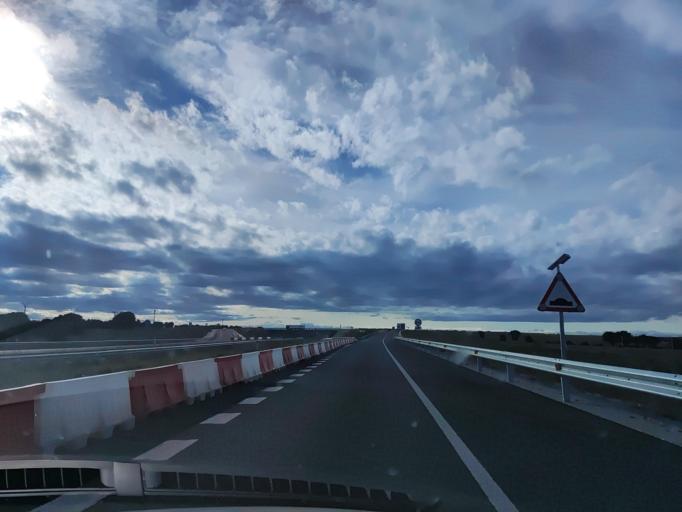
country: ES
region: Castille and Leon
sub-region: Provincia de Salamanca
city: Fuentes de Onoro
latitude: 40.5935
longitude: -6.7918
